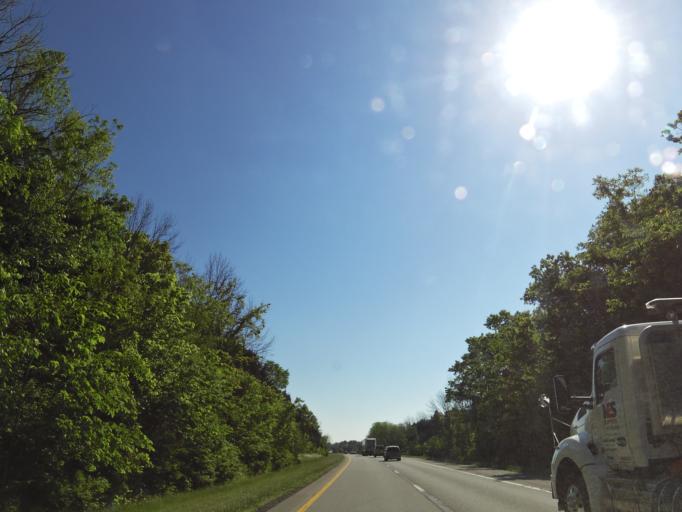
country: US
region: Kentucky
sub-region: Franklin County
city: Frankfort
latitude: 38.1527
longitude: -84.9372
